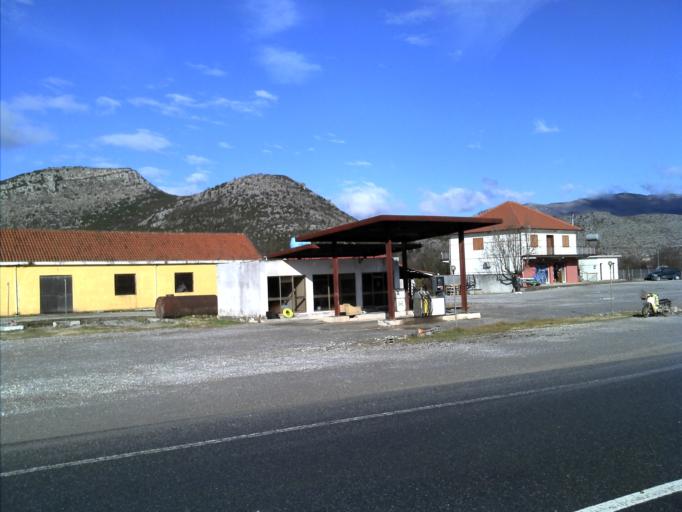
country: AL
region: Shkoder
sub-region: Rrethi i Malesia e Madhe
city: Hot
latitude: 42.3073
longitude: 19.4408
